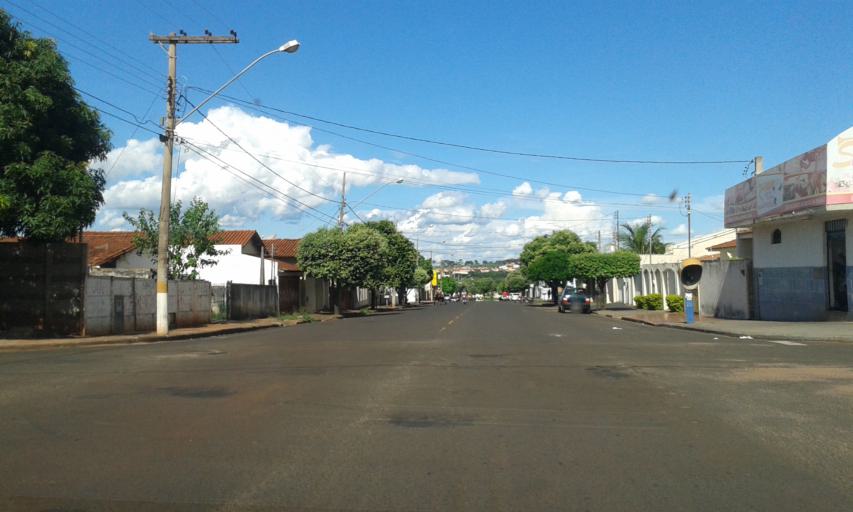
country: BR
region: Minas Gerais
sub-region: Ituiutaba
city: Ituiutaba
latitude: -18.9815
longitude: -49.4550
